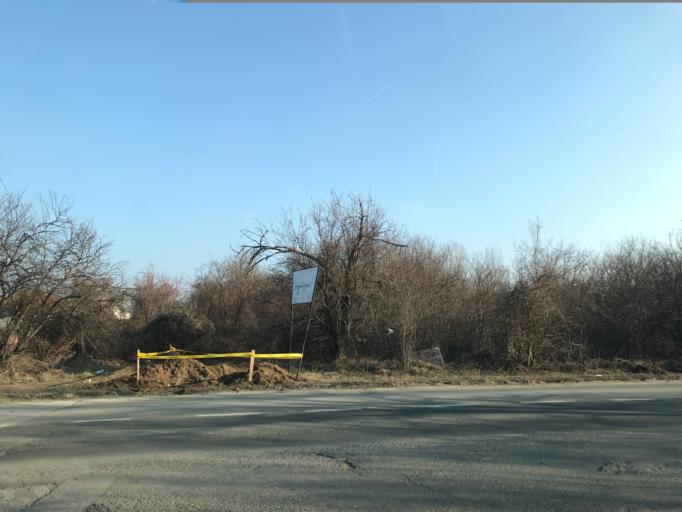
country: RS
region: Autonomna Pokrajina Vojvodina
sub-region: Juznobacki Okrug
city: Petrovaradin
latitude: 45.2253
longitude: 19.8562
